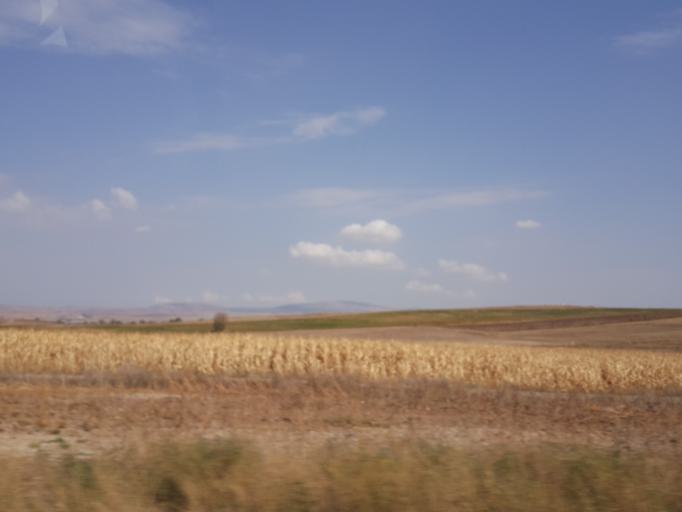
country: TR
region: Corum
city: Alaca
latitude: 40.1488
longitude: 34.8847
